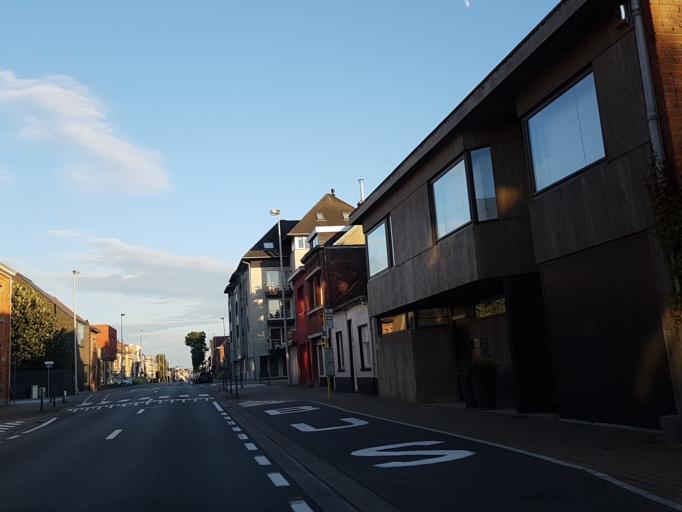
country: BE
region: Flanders
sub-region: Provincie Oost-Vlaanderen
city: Dendermonde
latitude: 51.0161
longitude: 4.1135
